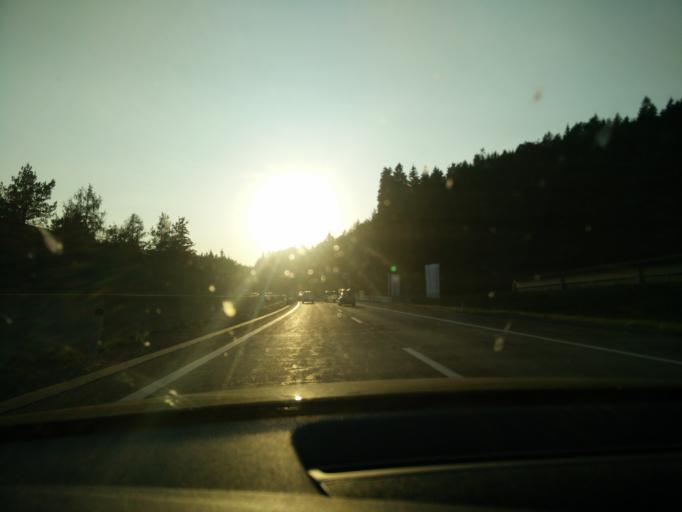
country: AT
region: Carinthia
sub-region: Politischer Bezirk Klagenfurt Land
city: Maria Worth
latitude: 46.6408
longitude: 14.1384
